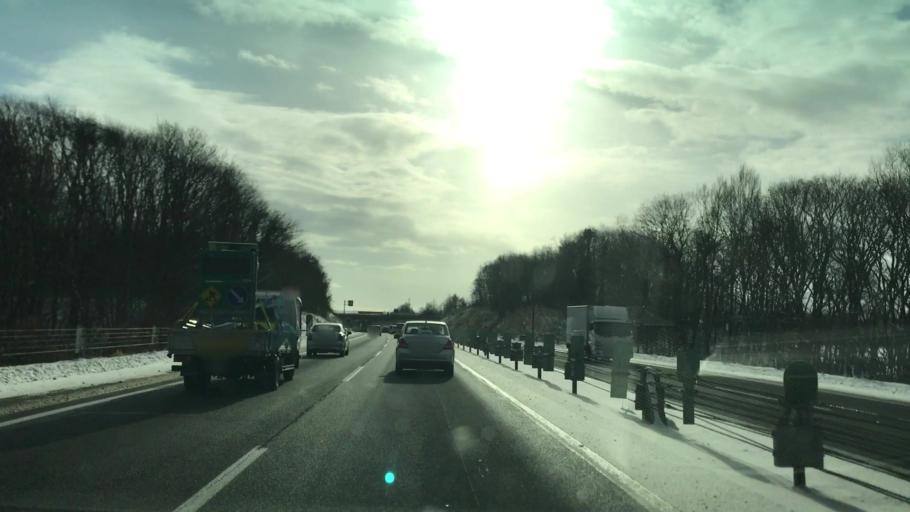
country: JP
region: Hokkaido
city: Kitahiroshima
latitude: 42.9396
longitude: 141.5222
